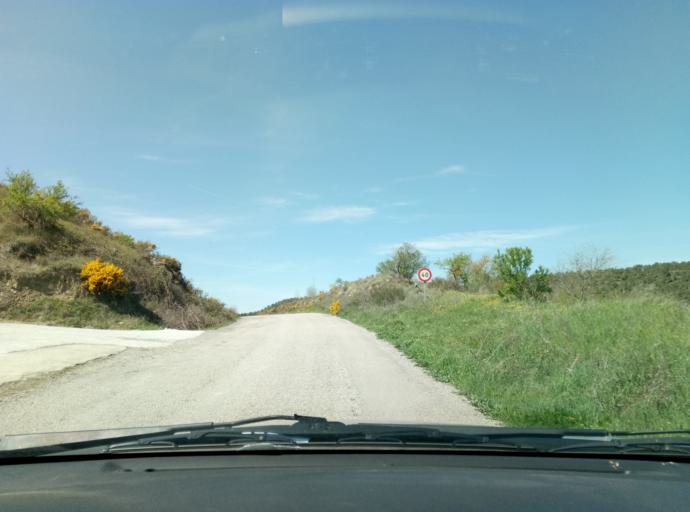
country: ES
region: Catalonia
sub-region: Provincia de Lleida
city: Fulleda
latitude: 41.4934
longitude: 0.9969
